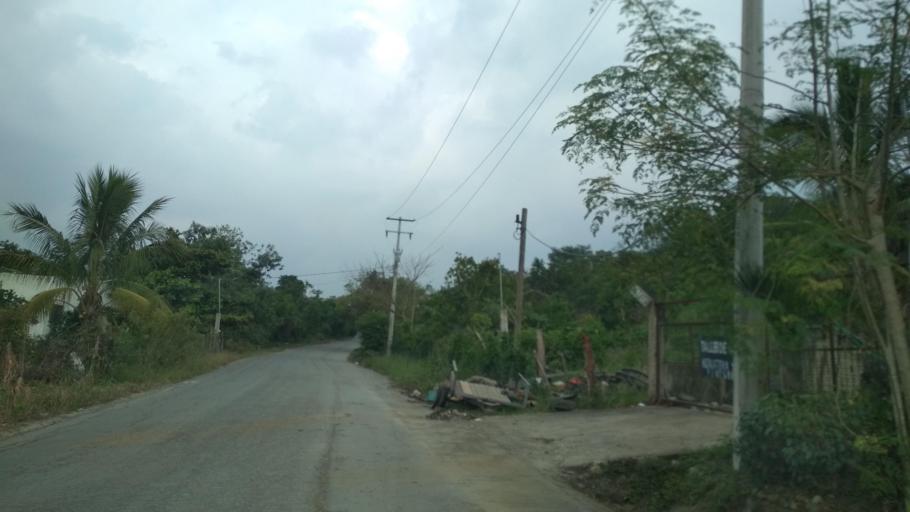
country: MM
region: Kayah
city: Loikaw
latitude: 20.2410
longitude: 97.2748
